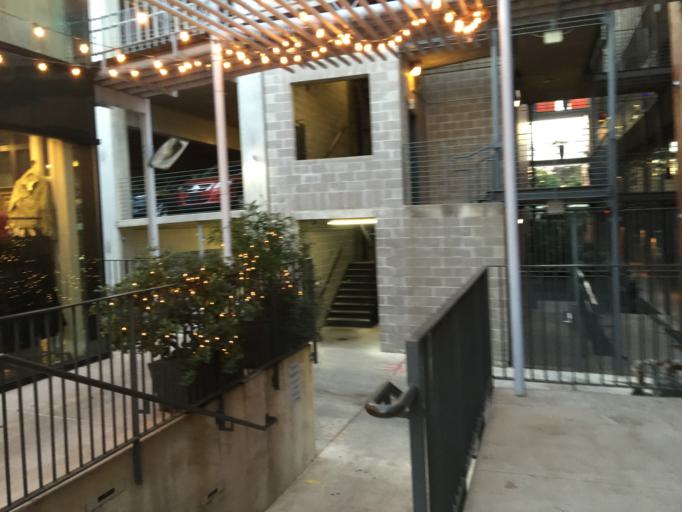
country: US
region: Texas
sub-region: Travis County
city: Austin
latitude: 30.2499
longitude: -97.7502
